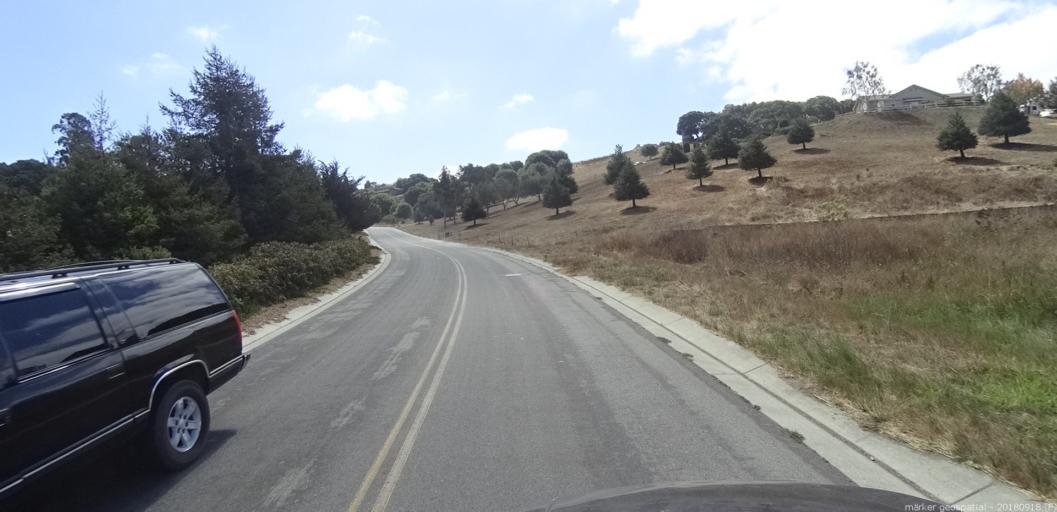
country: US
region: California
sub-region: Monterey County
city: Prunedale
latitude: 36.7658
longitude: -121.6649
